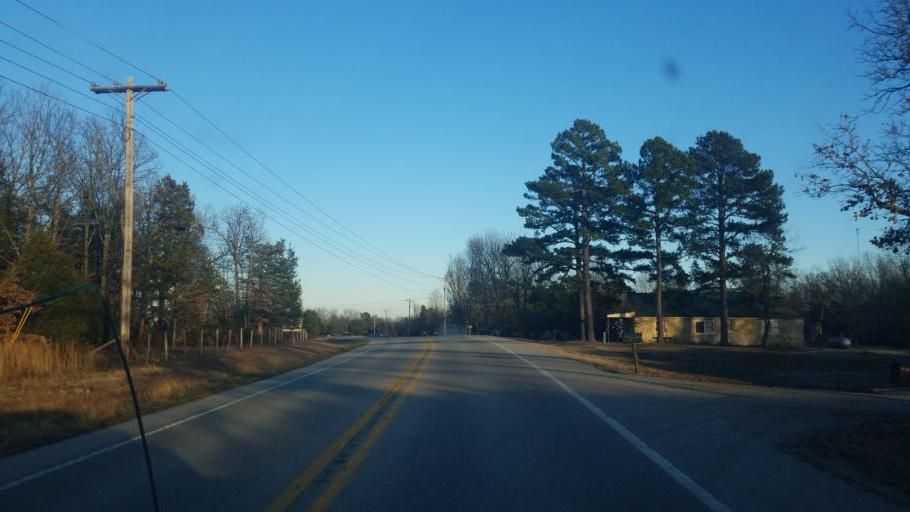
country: US
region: Arkansas
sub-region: Baxter County
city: Mountain Home
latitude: 36.3839
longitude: -92.1690
